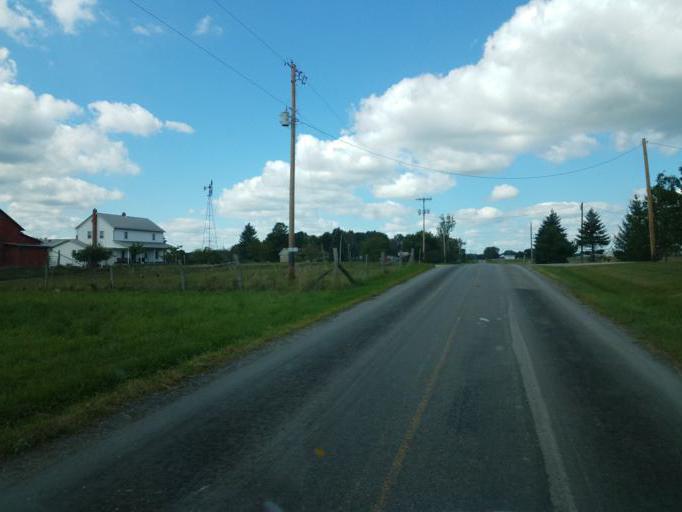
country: US
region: Ohio
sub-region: Wayne County
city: West Salem
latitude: 41.0425
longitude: -82.1161
